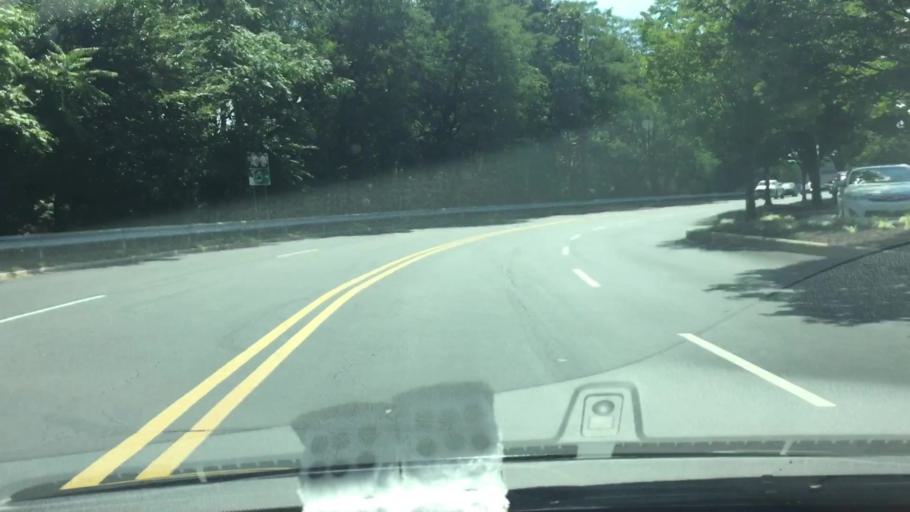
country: US
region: New Jersey
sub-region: Camden County
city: Glendora
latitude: 39.8313
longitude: -75.0951
